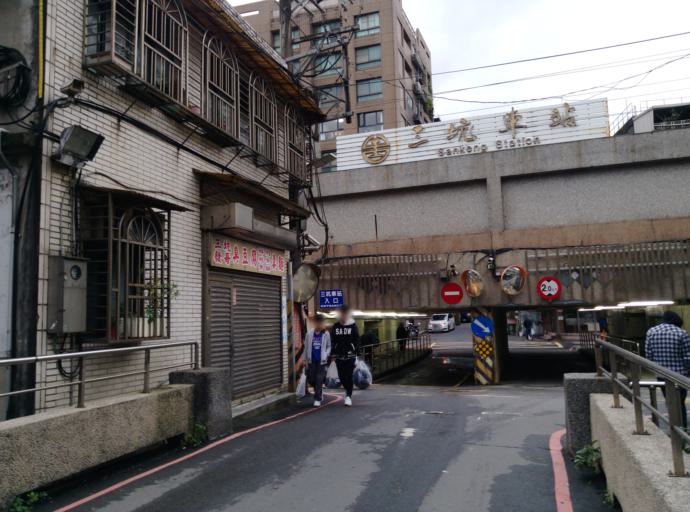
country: TW
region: Taiwan
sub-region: Keelung
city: Keelung
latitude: 25.1229
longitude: 121.7417
